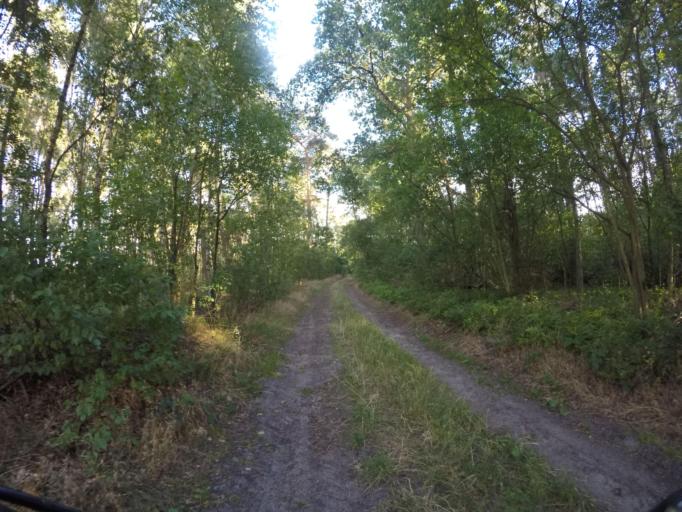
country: DE
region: Lower Saxony
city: Hitzacker
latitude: 53.2229
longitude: 11.0551
